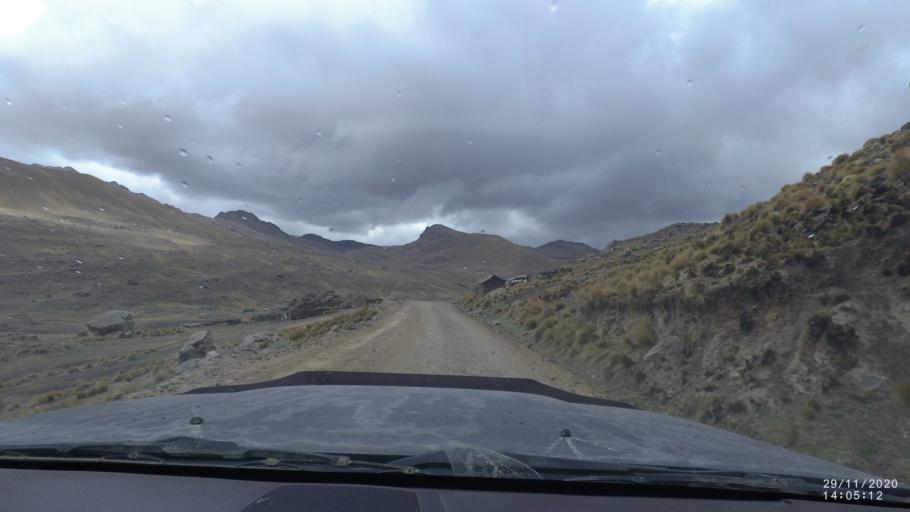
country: BO
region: Cochabamba
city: Sipe Sipe
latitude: -17.2052
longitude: -66.3774
